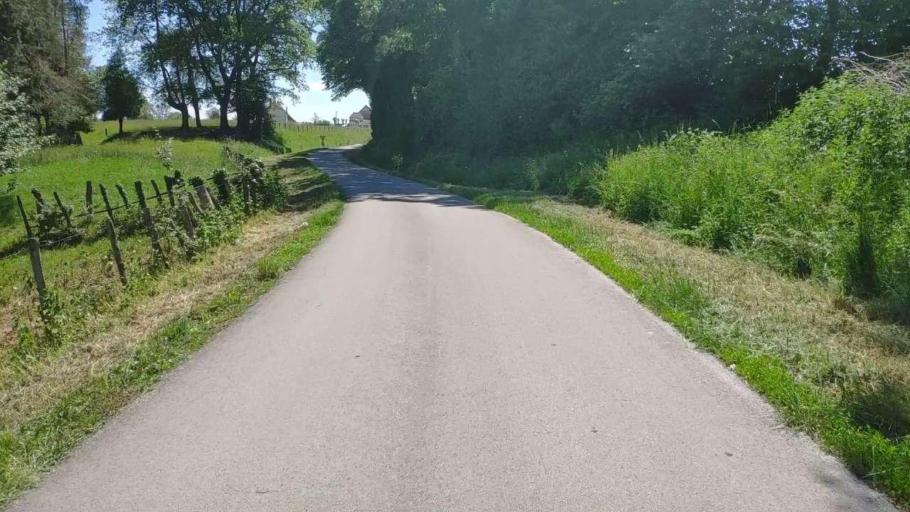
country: FR
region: Franche-Comte
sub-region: Departement du Jura
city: Bletterans
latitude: 46.7442
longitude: 5.3891
